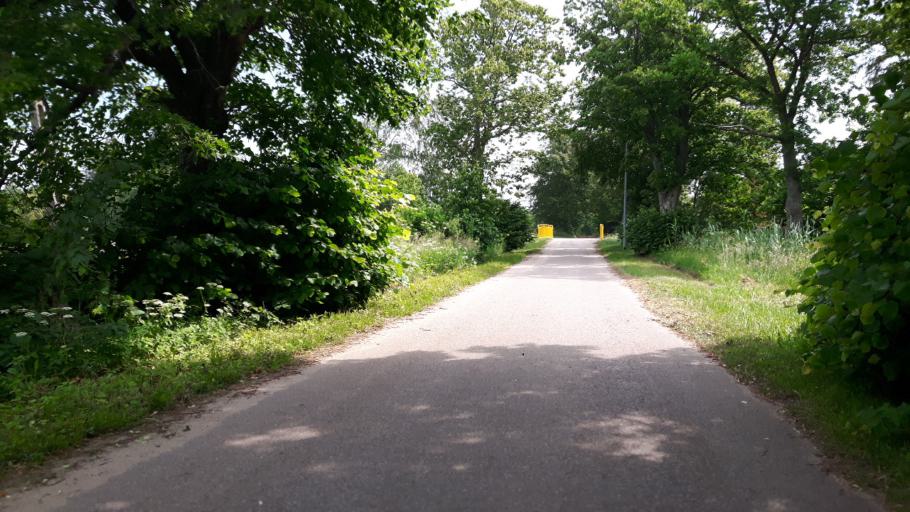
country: PL
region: Pomeranian Voivodeship
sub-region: Powiat leborski
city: Leba
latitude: 54.7532
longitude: 17.6108
